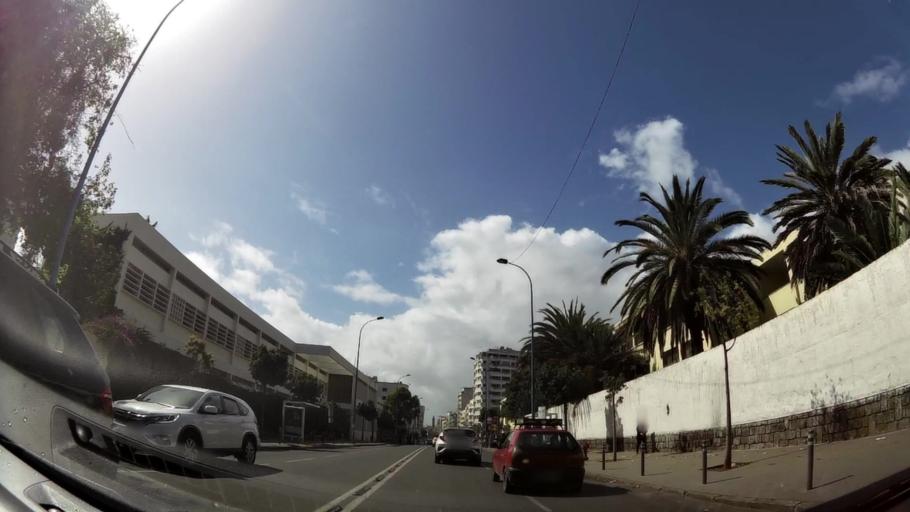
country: MA
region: Grand Casablanca
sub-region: Casablanca
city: Casablanca
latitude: 33.5784
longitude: -7.6153
